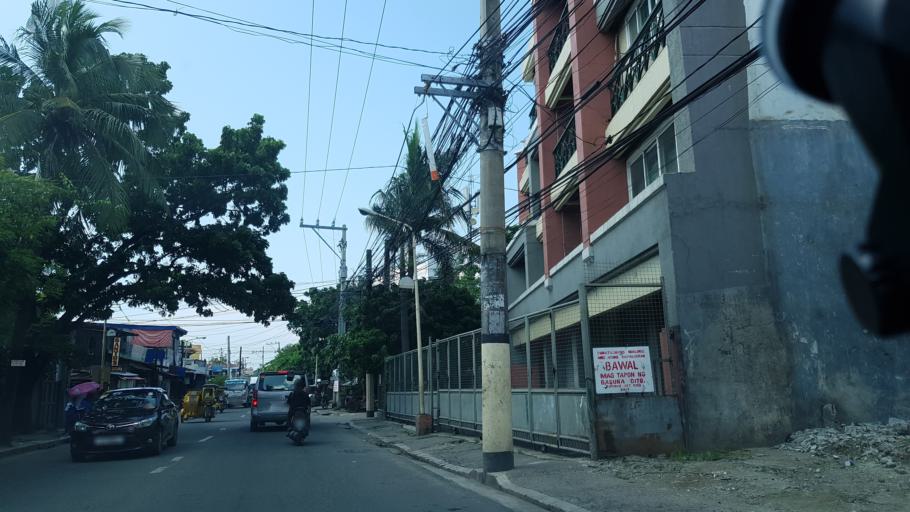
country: PH
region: Calabarzon
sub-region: Province of Rizal
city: Las Pinas
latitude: 14.4692
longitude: 120.9797
